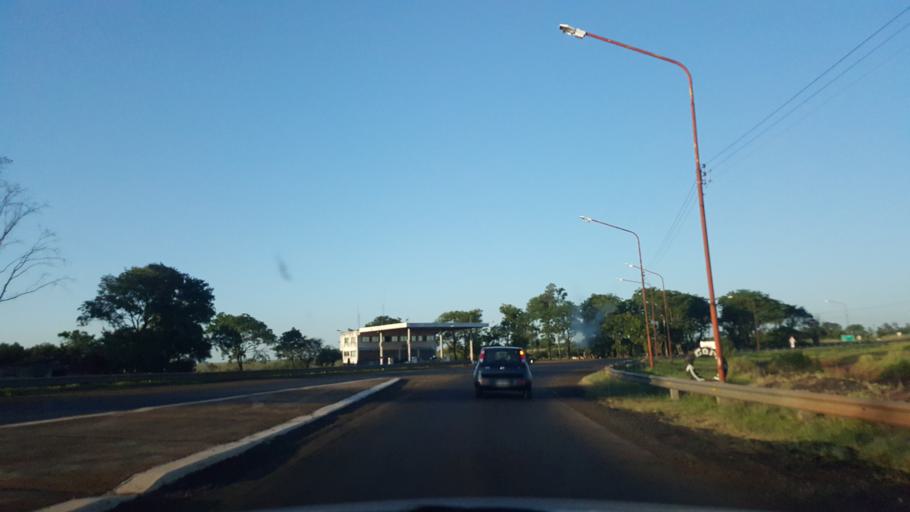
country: AR
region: Corrientes
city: Santo Tome
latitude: -28.3590
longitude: -56.1139
